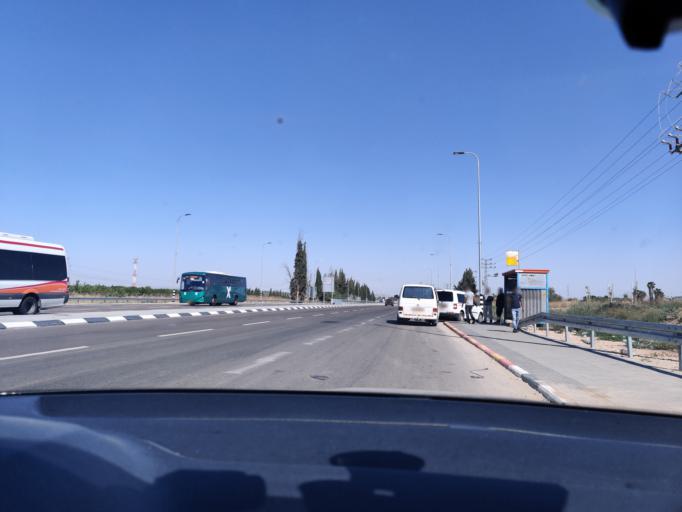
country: IL
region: Southern District
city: Qiryat Gat
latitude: 31.6080
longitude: 34.7872
